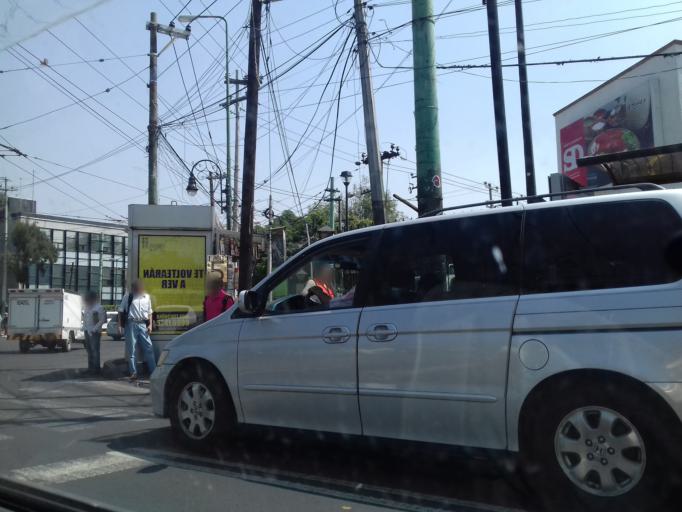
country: MX
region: Mexico City
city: Coyoacan
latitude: 19.3466
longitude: -99.1806
